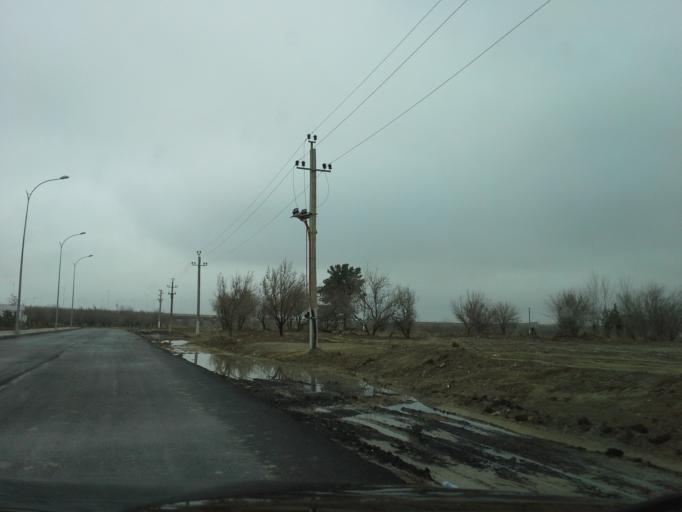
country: TM
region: Ahal
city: Ashgabat
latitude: 37.9747
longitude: 58.4007
